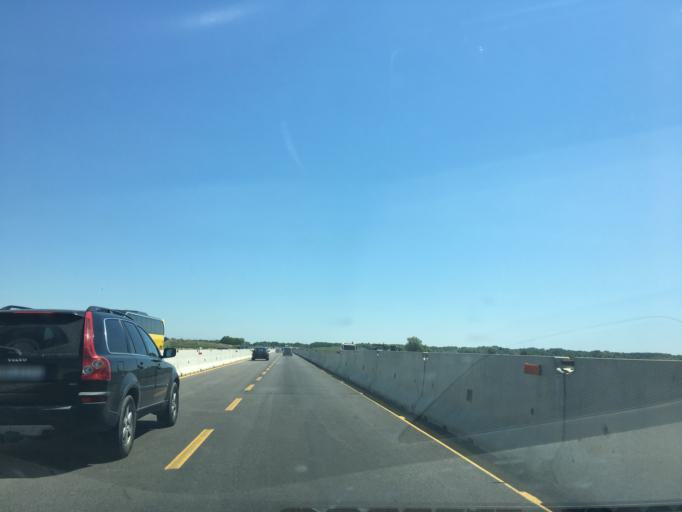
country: IT
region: Veneto
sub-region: Provincia di Venezia
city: San Giorgio al Tagliamento-Pozzi
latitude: 45.8082
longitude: 12.9502
